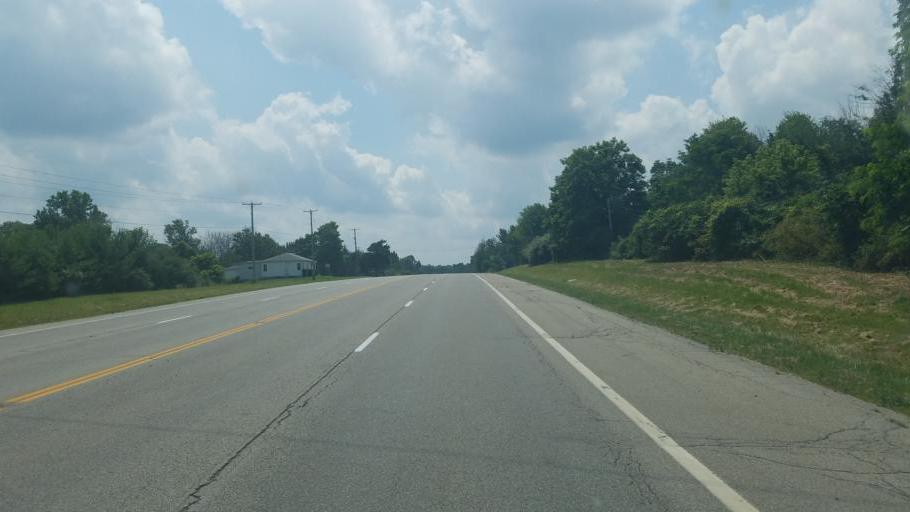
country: US
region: Ohio
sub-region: Richland County
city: Ontario
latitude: 40.7982
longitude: -82.5699
